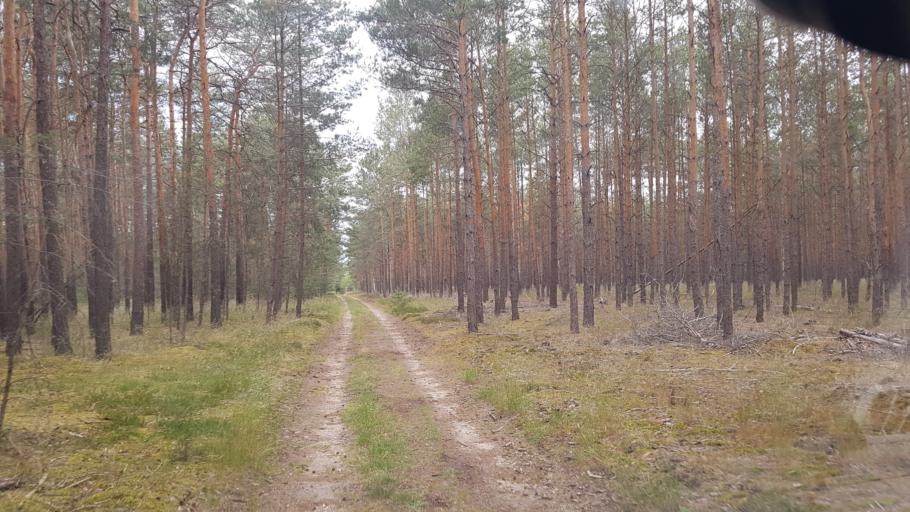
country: DE
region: Brandenburg
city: Finsterwalde
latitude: 51.6188
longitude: 13.6396
